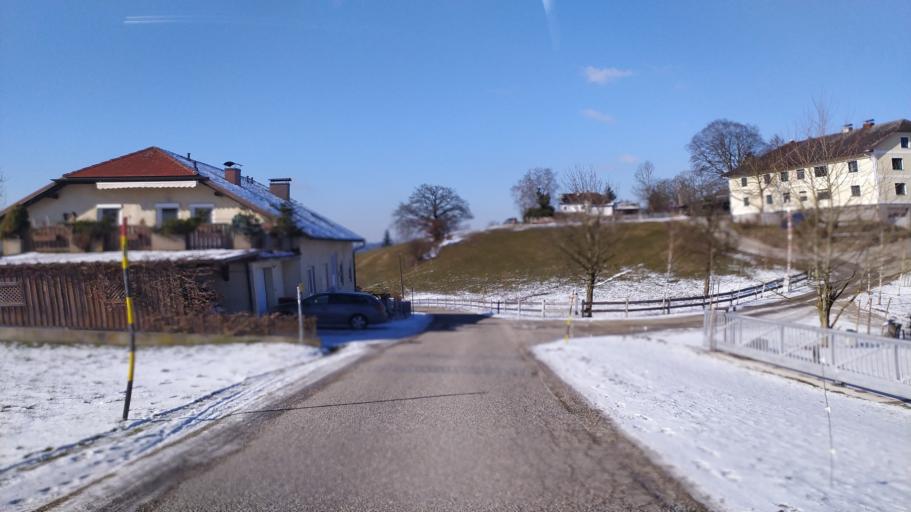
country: AT
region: Upper Austria
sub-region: Politischer Bezirk Urfahr-Umgebung
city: Ottensheim
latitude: 48.3453
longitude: 14.2058
